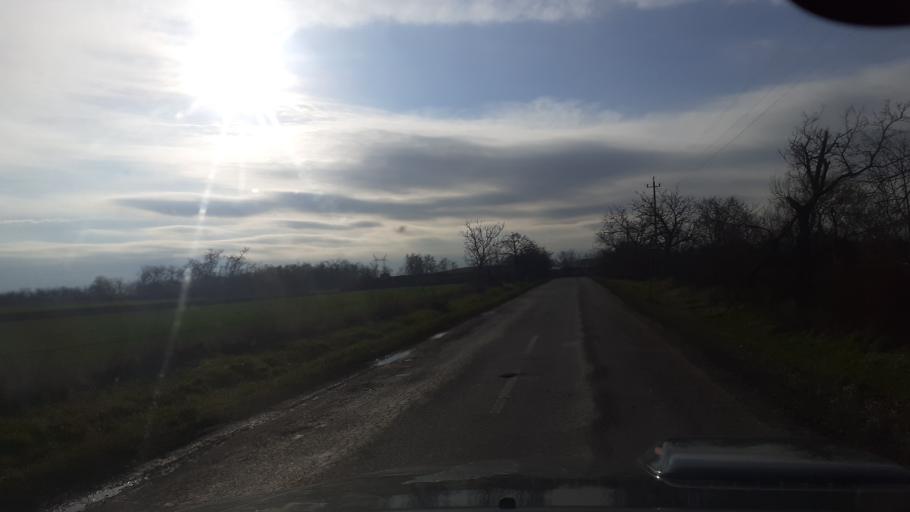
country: HU
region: Pest
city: Domsod
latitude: 47.0901
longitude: 19.0393
